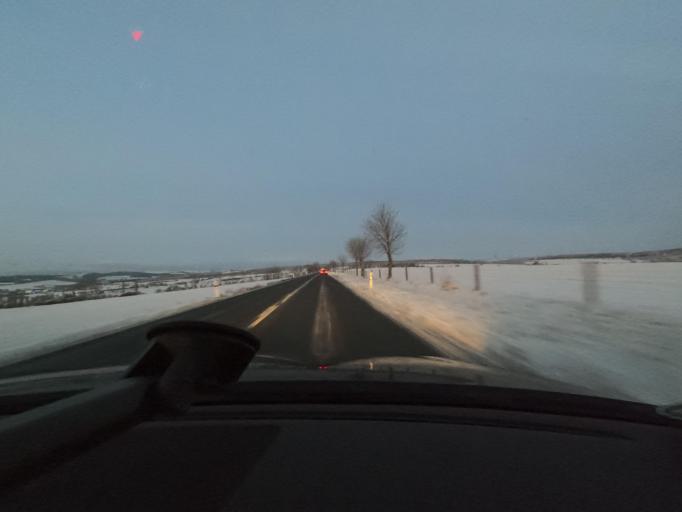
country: DE
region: Thuringia
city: Muehlhausen
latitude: 51.2680
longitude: 10.4157
